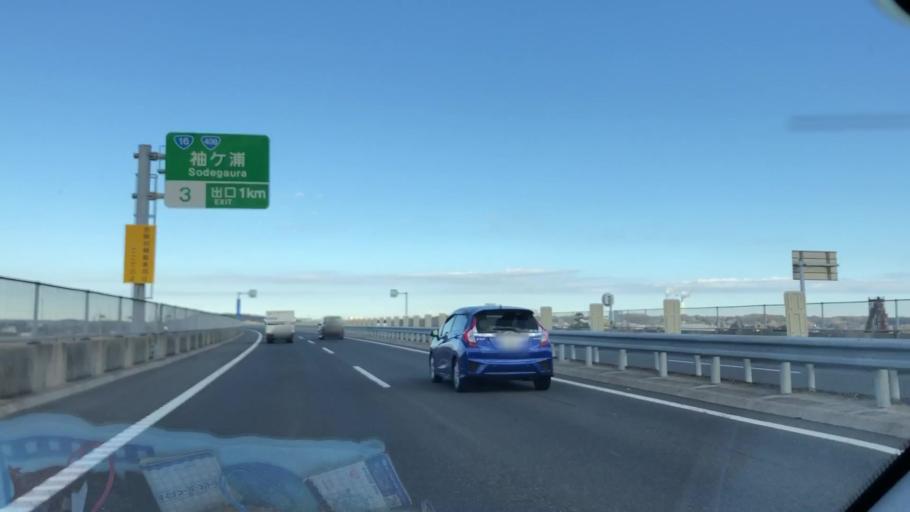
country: JP
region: Chiba
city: Kisarazu
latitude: 35.4015
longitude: 139.9665
